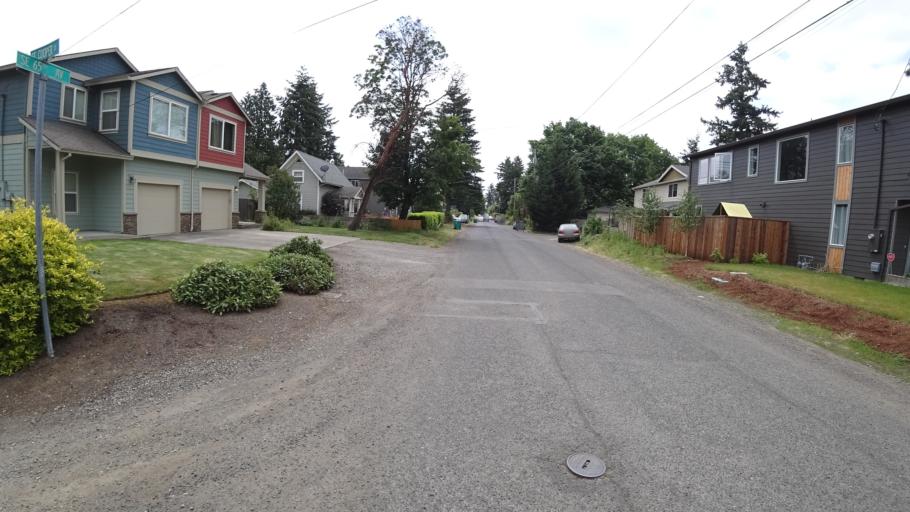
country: US
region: Oregon
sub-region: Multnomah County
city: Lents
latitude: 45.4734
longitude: -122.5962
